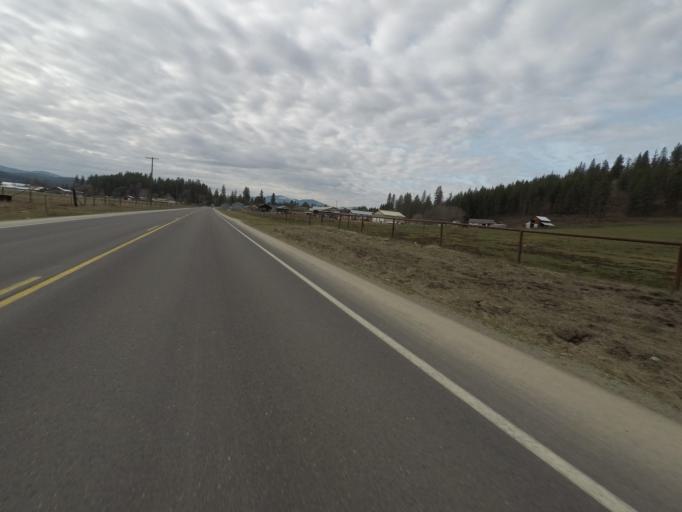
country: US
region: Washington
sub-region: Stevens County
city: Colville
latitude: 48.5622
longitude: -117.8797
